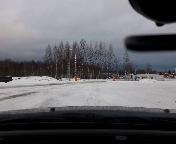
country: SE
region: Gaevleborg
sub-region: Bollnas Kommun
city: Bollnas
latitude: 61.3396
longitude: 16.3862
